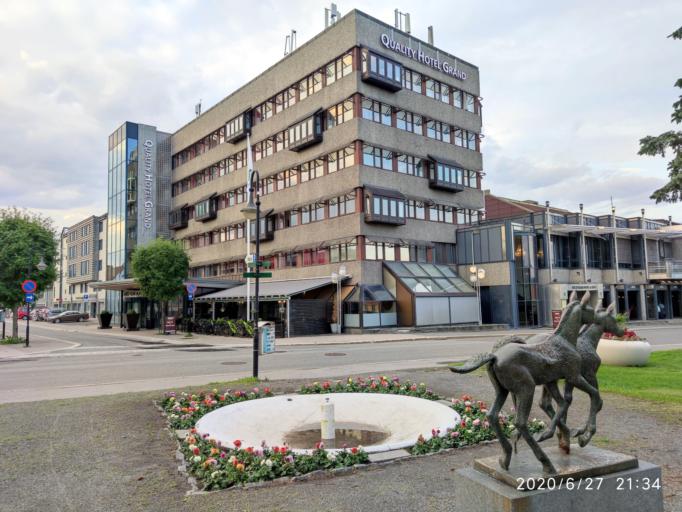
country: NO
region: Buskerud
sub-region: Kongsberg
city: Kongsberg
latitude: 59.6689
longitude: 9.6489
